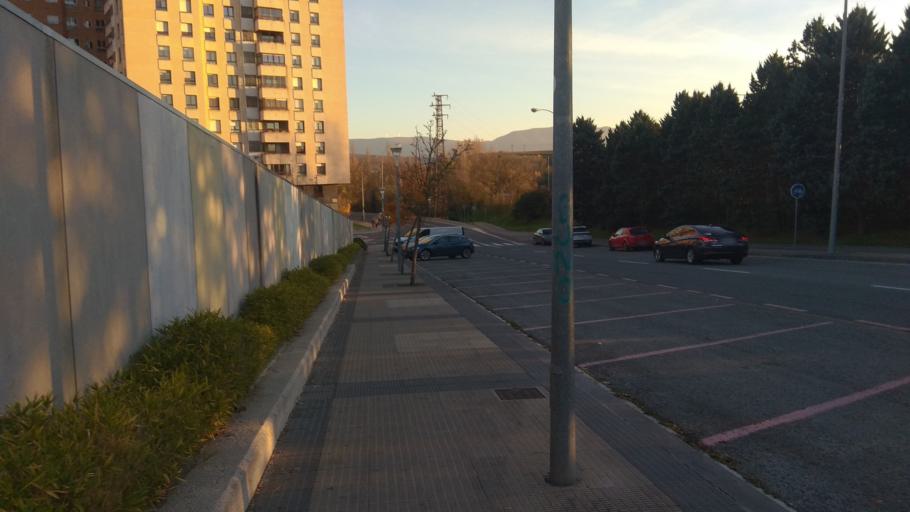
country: ES
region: Navarre
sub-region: Provincia de Navarra
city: Iturrama
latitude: 42.8013
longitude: -1.6485
